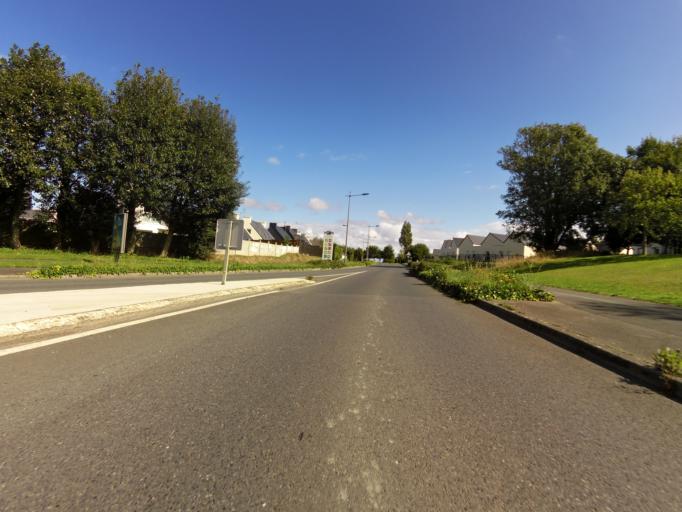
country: FR
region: Brittany
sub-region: Departement des Cotes-d'Armor
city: Langueux
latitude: 48.4855
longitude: -2.7425
